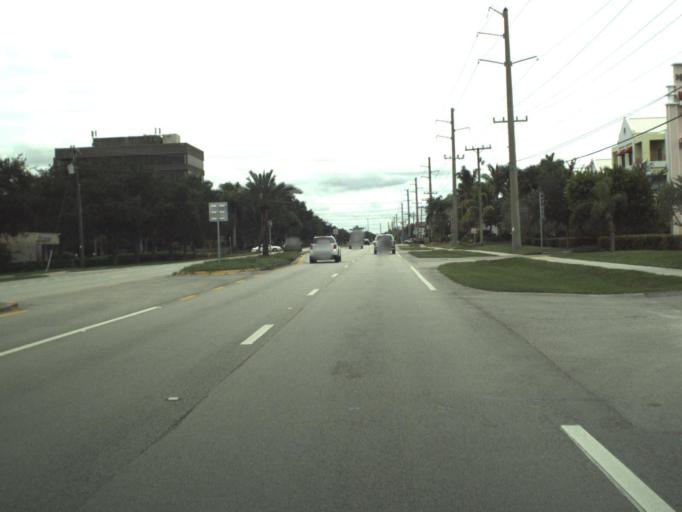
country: US
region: Florida
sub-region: Palm Beach County
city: Juno Beach
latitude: 26.8516
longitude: -80.0589
